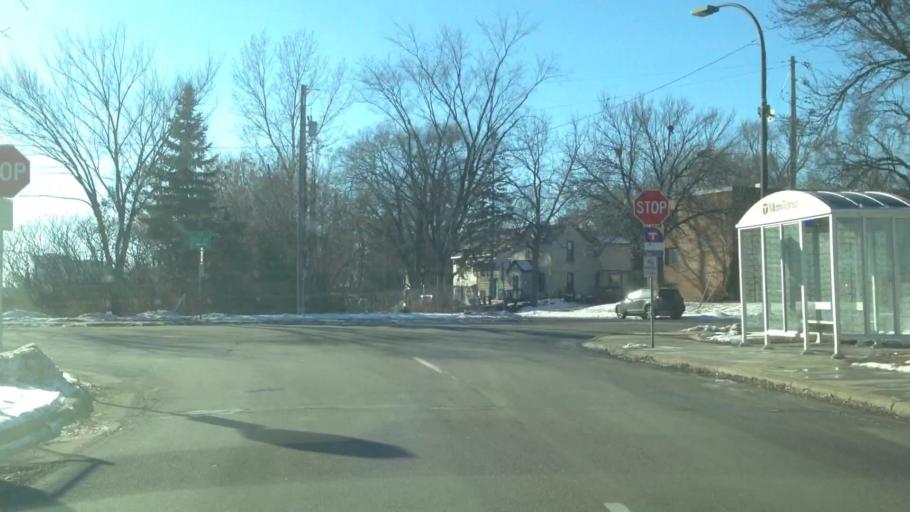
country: US
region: Minnesota
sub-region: Hennepin County
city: Minneapolis
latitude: 44.9873
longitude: -93.2391
